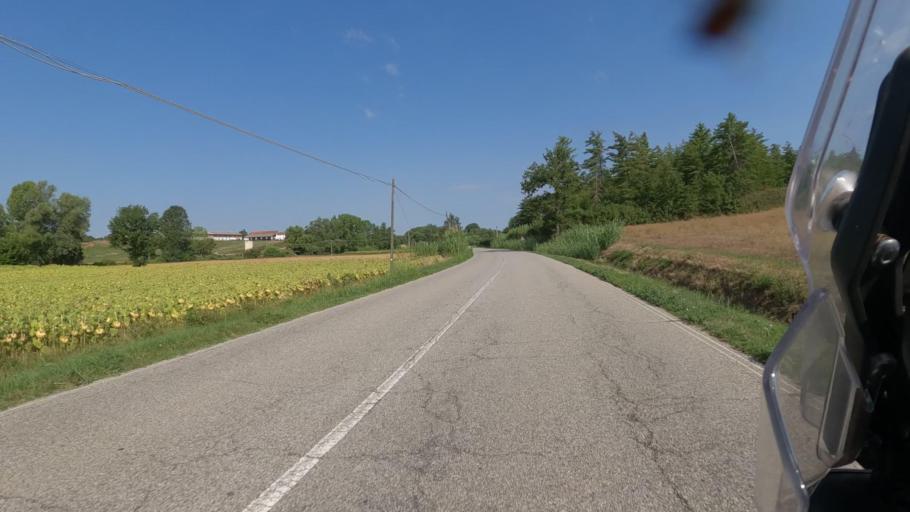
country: IT
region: Piedmont
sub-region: Provincia di Alessandria
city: Quattordio
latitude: 44.9103
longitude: 8.3981
